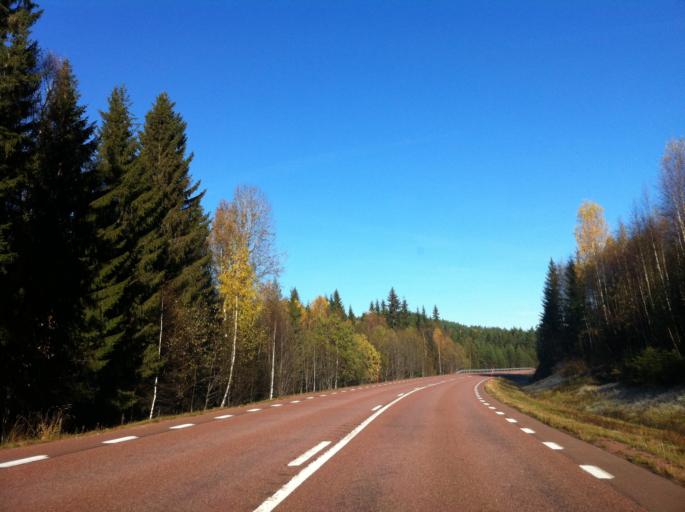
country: SE
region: Dalarna
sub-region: Alvdalens Kommun
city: AElvdalen
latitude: 61.2713
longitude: 13.8373
